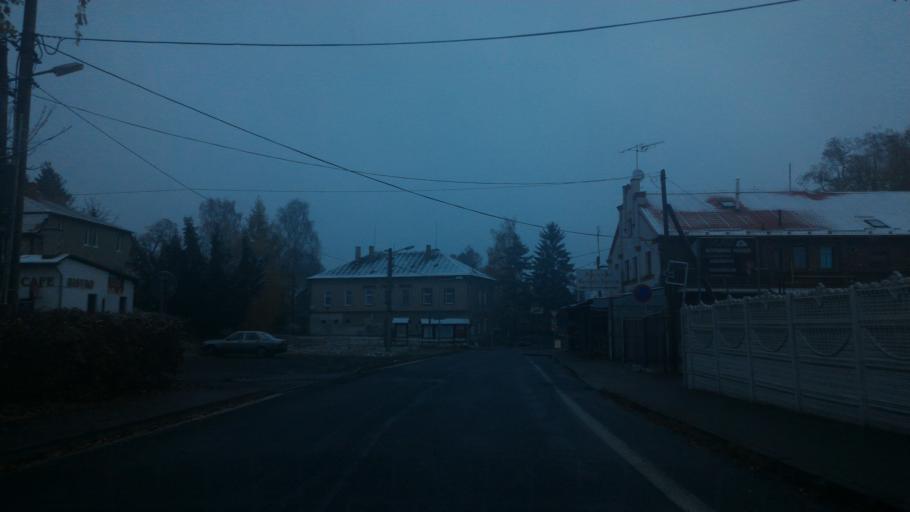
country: CZ
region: Ustecky
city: Jirikov
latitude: 51.0012
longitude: 14.5745
